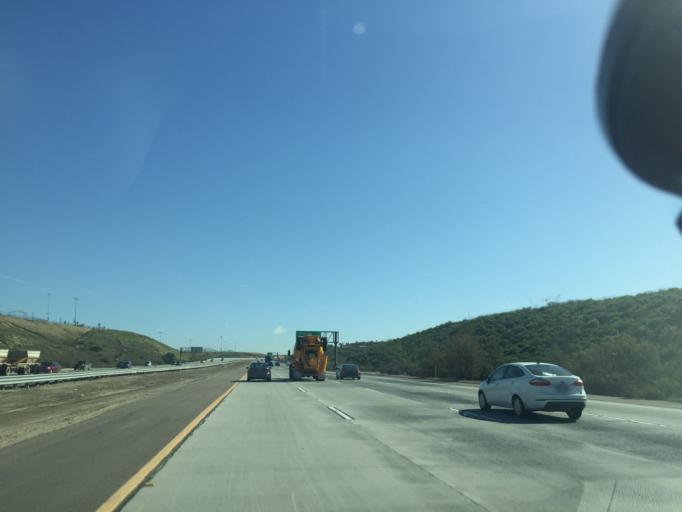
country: MX
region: Baja California
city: Tijuana
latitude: 32.5681
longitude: -117.0304
